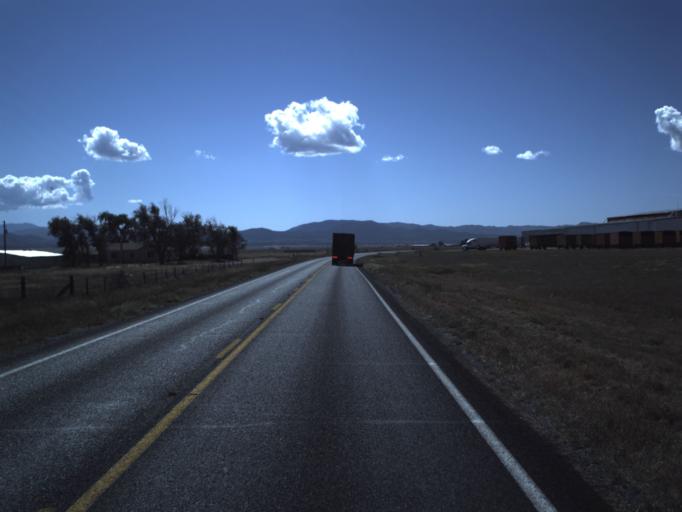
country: US
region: Utah
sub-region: Washington County
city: Enterprise
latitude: 37.6801
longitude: -113.6565
